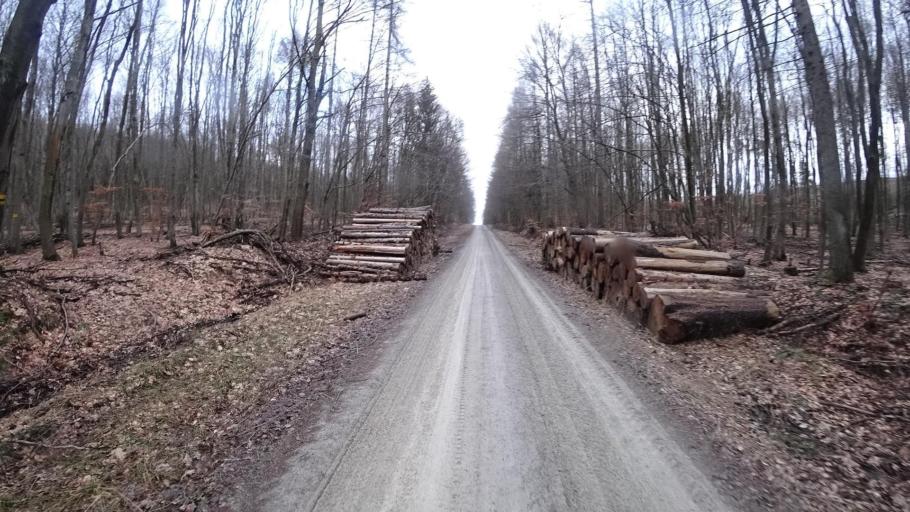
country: DE
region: Rheinland-Pfalz
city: Dernbach
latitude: 50.4243
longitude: 7.7640
